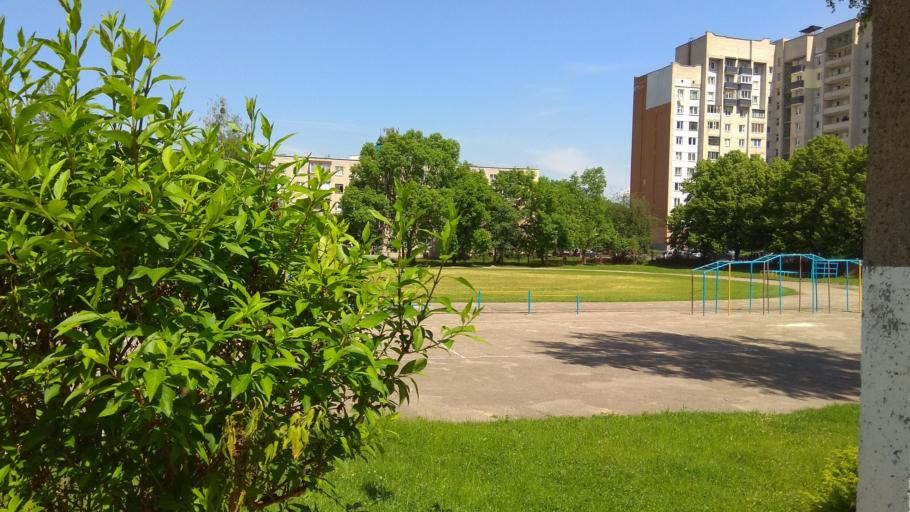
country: BY
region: Grodnenskaya
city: Hrodna
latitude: 53.7079
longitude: 23.8011
